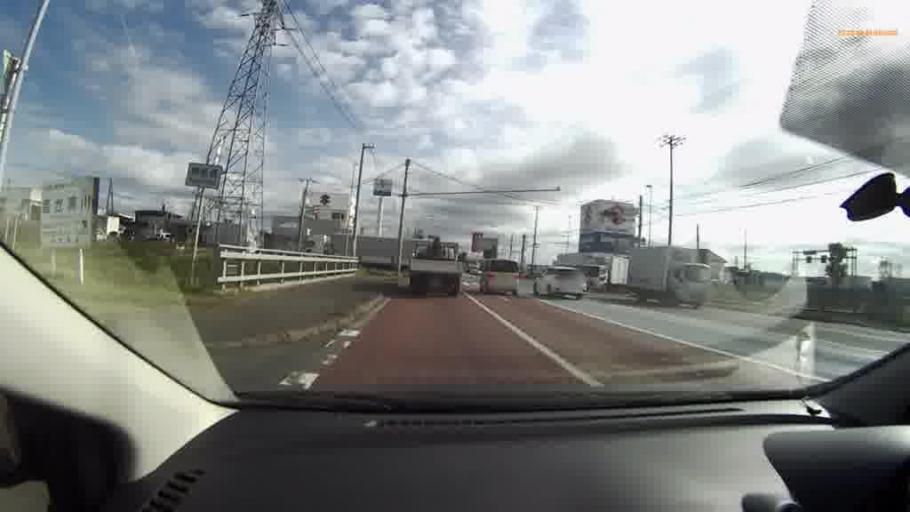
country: JP
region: Hokkaido
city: Kushiro
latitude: 43.0130
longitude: 144.3073
